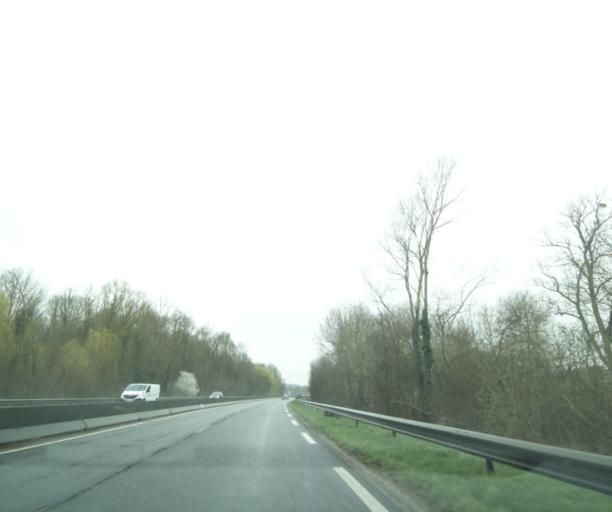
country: FR
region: Ile-de-France
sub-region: Departement de l'Essonne
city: Morigny-Champigny
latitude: 48.4423
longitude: 2.1750
